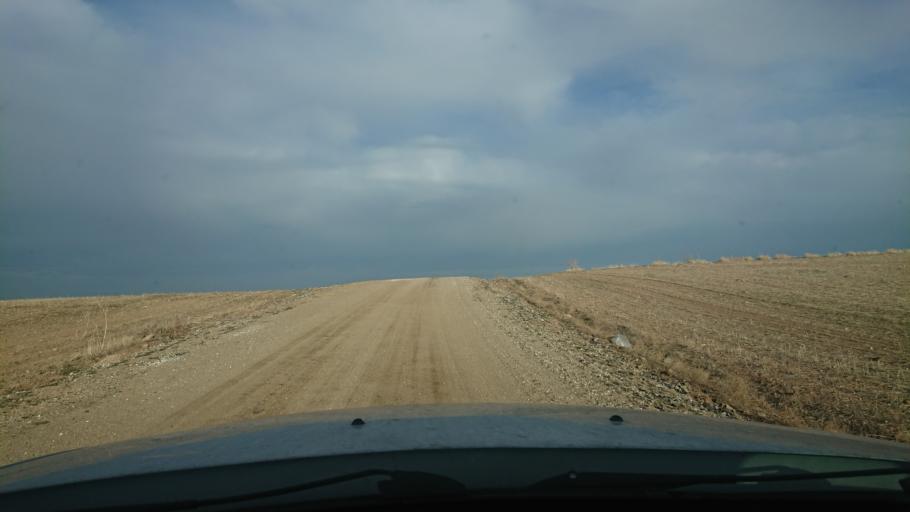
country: TR
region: Aksaray
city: Ortakoy
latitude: 38.7032
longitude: 33.8727
